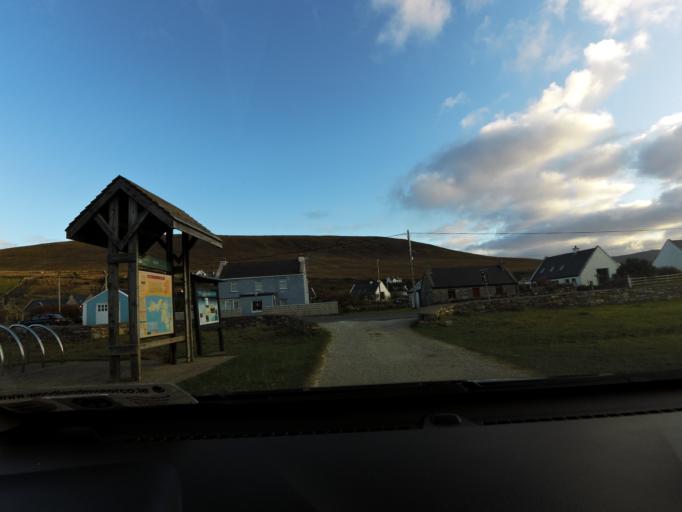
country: IE
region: Connaught
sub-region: Maigh Eo
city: Belmullet
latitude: 54.0107
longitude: -10.0229
